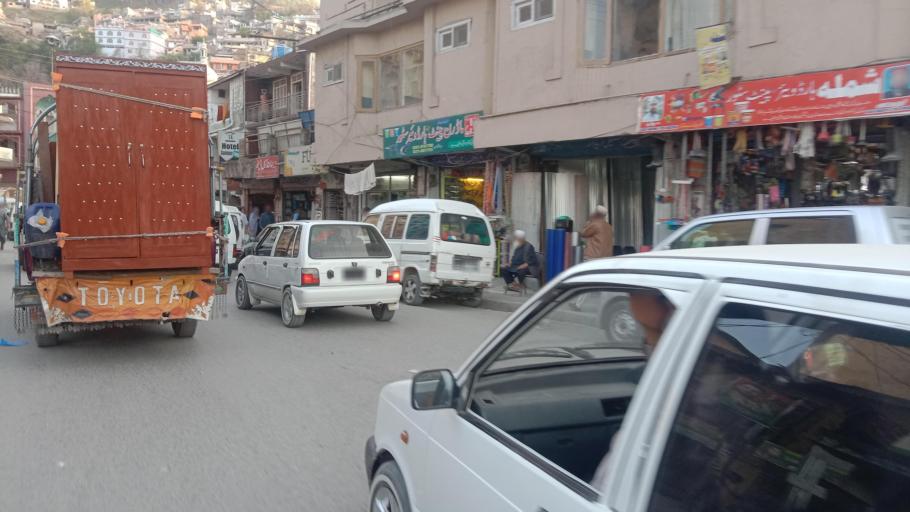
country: PK
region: Khyber Pakhtunkhwa
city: Abbottabad
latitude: 34.1413
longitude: 73.2136
